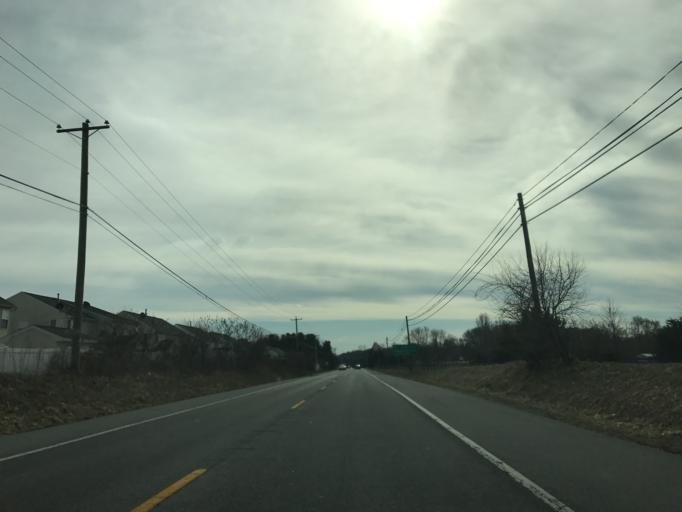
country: US
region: Maryland
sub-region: Queen Anne's County
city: Centreville
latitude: 39.0635
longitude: -76.0514
